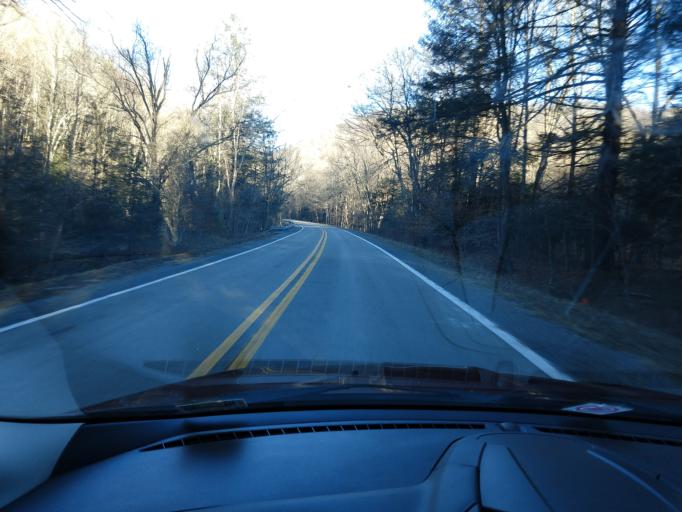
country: US
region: Virginia
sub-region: Highland County
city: Monterey
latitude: 38.5075
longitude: -79.7132
